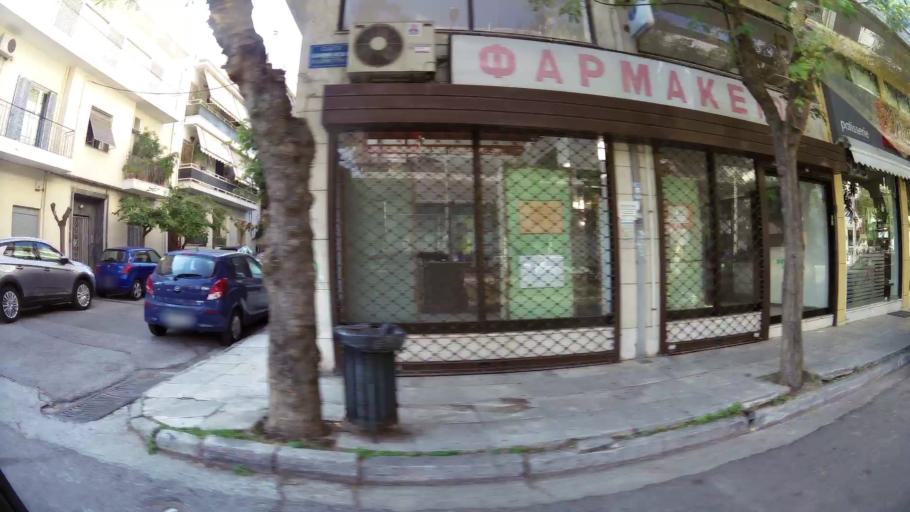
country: GR
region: Attica
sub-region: Nomarchia Athinas
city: Galatsi
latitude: 38.0244
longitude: 23.7454
